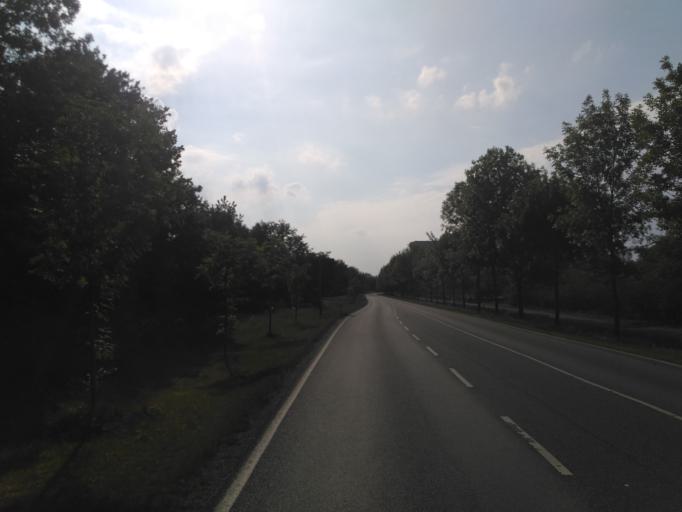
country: DE
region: Saxony
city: Hoyerswerda
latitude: 51.4302
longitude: 14.2643
